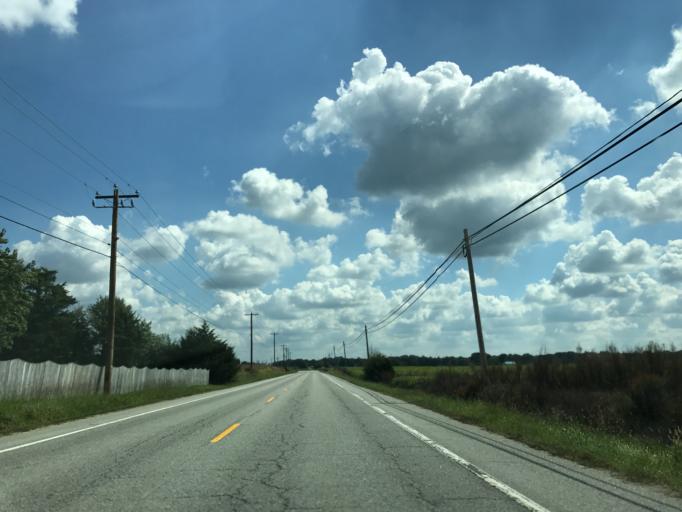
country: US
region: Maryland
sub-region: Queen Anne's County
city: Centreville
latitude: 39.0302
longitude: -76.0398
